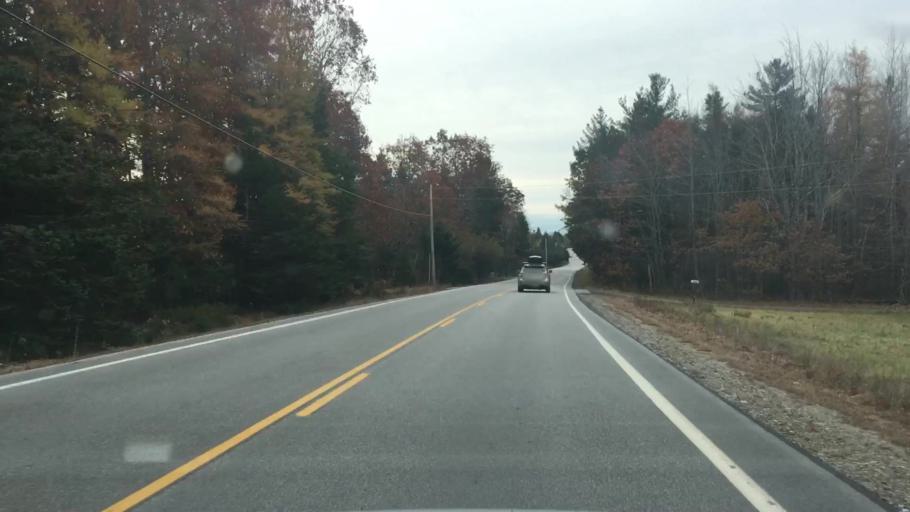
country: US
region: Maine
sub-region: Hancock County
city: Penobscot
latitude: 44.4771
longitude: -68.6379
